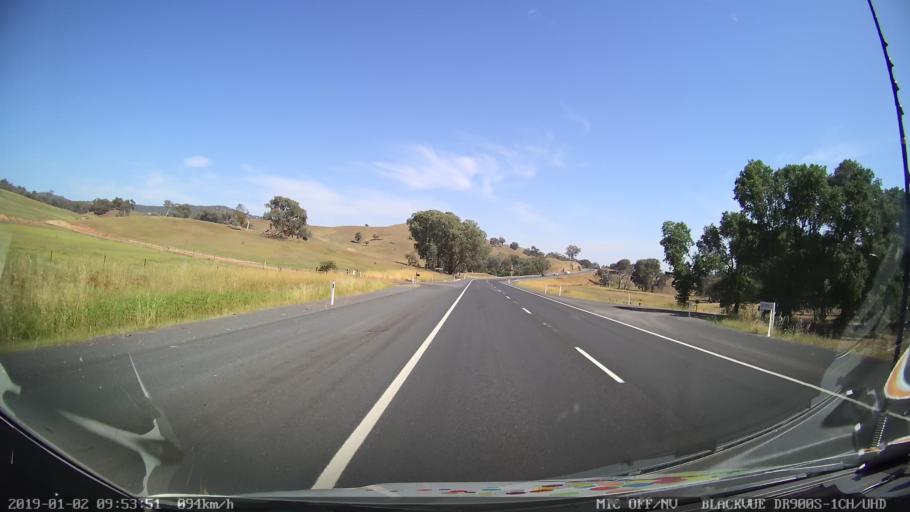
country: AU
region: New South Wales
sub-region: Tumut Shire
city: Tumut
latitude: -35.2430
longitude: 148.1996
